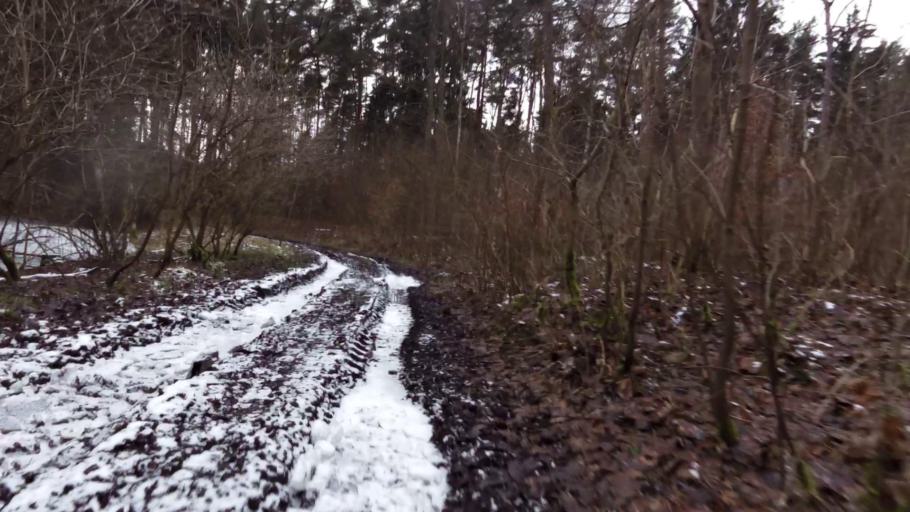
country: PL
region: West Pomeranian Voivodeship
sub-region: Powiat drawski
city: Drawsko Pomorskie
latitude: 53.5417
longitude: 15.7008
